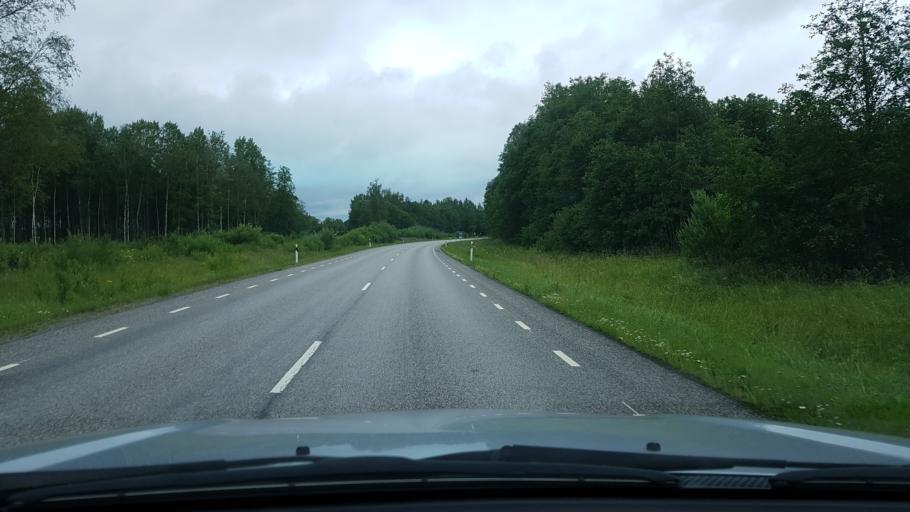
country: EE
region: Ida-Virumaa
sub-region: Narva-Joesuu linn
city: Narva-Joesuu
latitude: 59.3476
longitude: 27.9324
